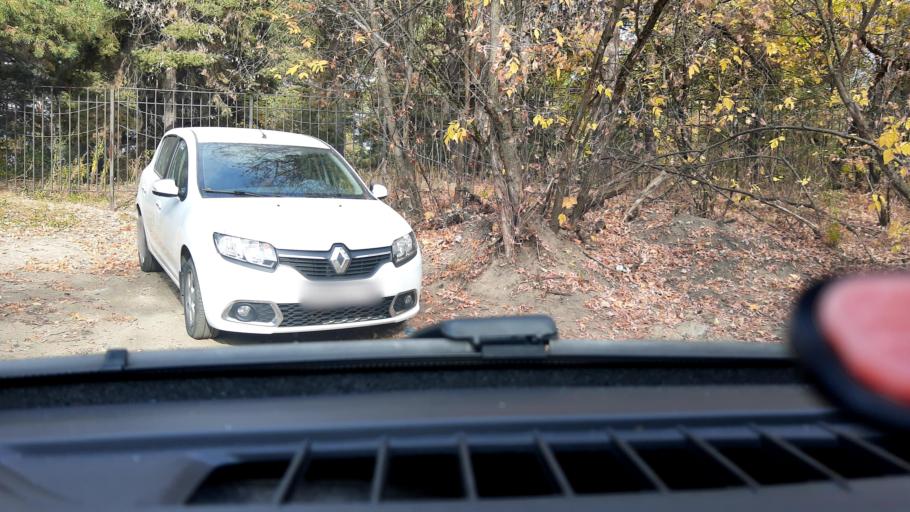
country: RU
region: Nizjnij Novgorod
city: Gorbatovka
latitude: 56.3340
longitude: 43.8582
